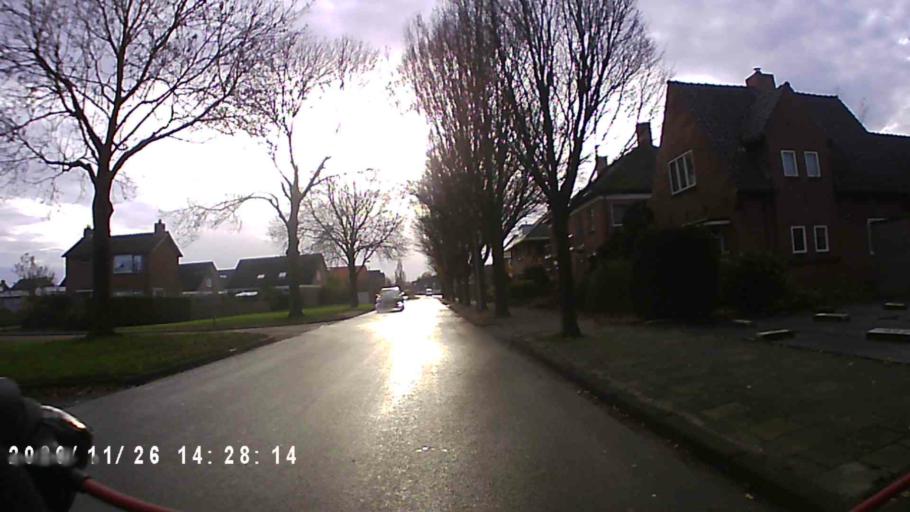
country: NL
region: Groningen
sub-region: Gemeente Appingedam
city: Appingedam
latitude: 53.3192
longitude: 6.8684
